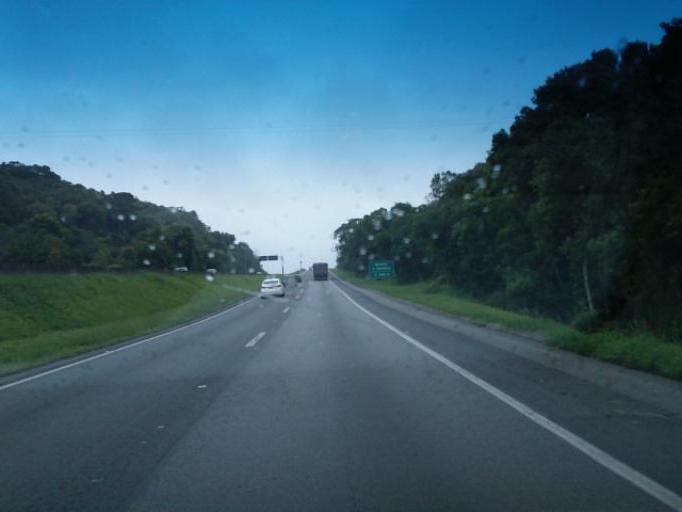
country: BR
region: Parana
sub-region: Campina Grande Do Sul
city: Campina Grande do Sul
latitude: -25.2742
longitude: -48.9221
